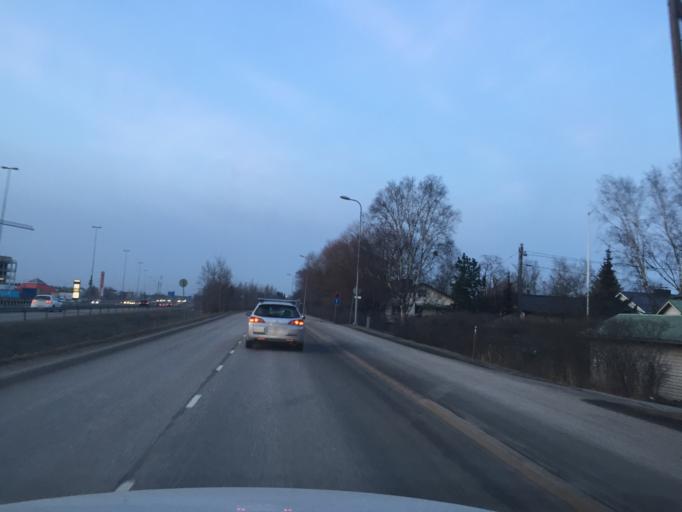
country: FI
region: Uusimaa
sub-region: Helsinki
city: Vantaa
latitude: 60.2760
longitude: 24.9773
